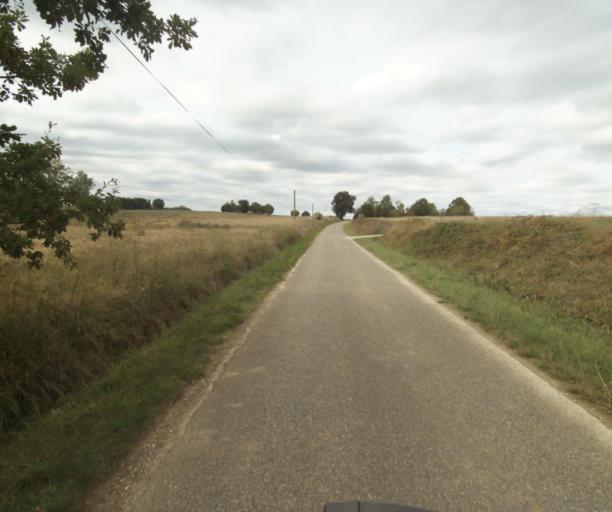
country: FR
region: Midi-Pyrenees
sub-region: Departement du Tarn-et-Garonne
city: Verdun-sur-Garonne
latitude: 43.8660
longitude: 1.1719
